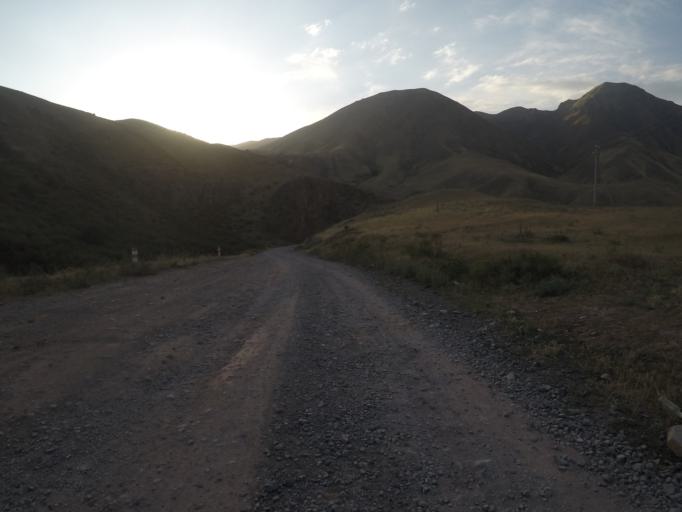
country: KG
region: Chuy
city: Bishkek
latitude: 42.6690
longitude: 74.6470
